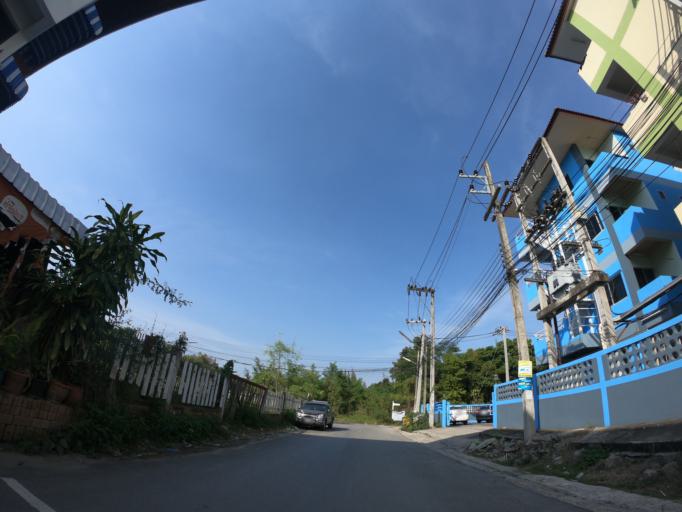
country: TH
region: Chiang Mai
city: Chiang Mai
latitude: 18.8178
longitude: 98.9884
